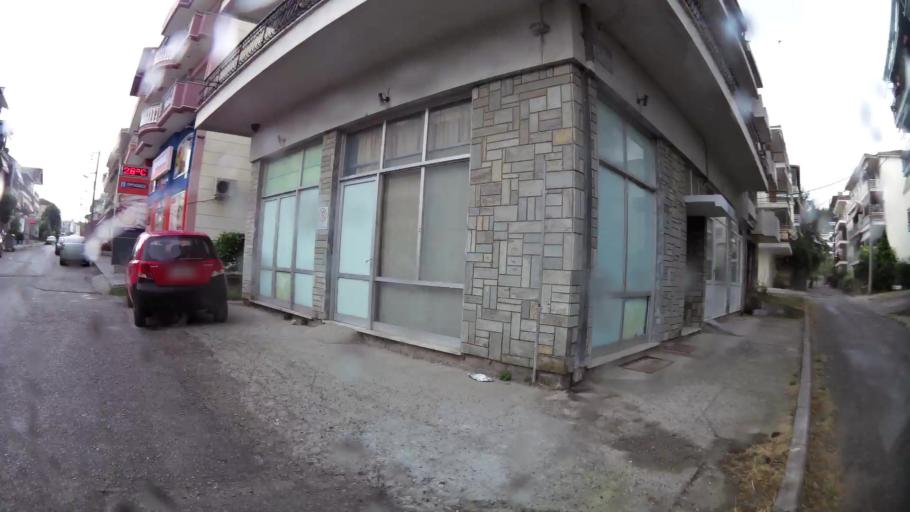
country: GR
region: Central Macedonia
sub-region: Nomos Imathias
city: Veroia
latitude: 40.5277
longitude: 22.1952
